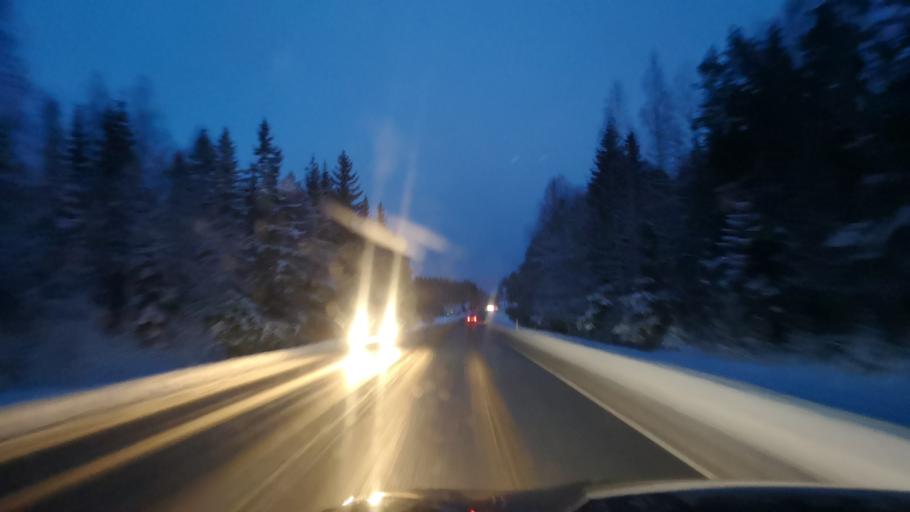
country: FI
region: Varsinais-Suomi
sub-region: Loimaa
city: Loimaa
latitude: 60.8722
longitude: 23.0632
